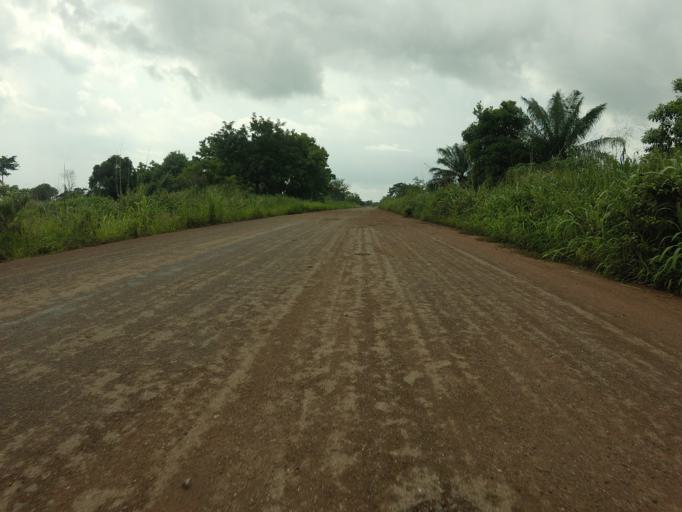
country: GH
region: Volta
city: Kpandu
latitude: 6.9429
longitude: 0.4611
